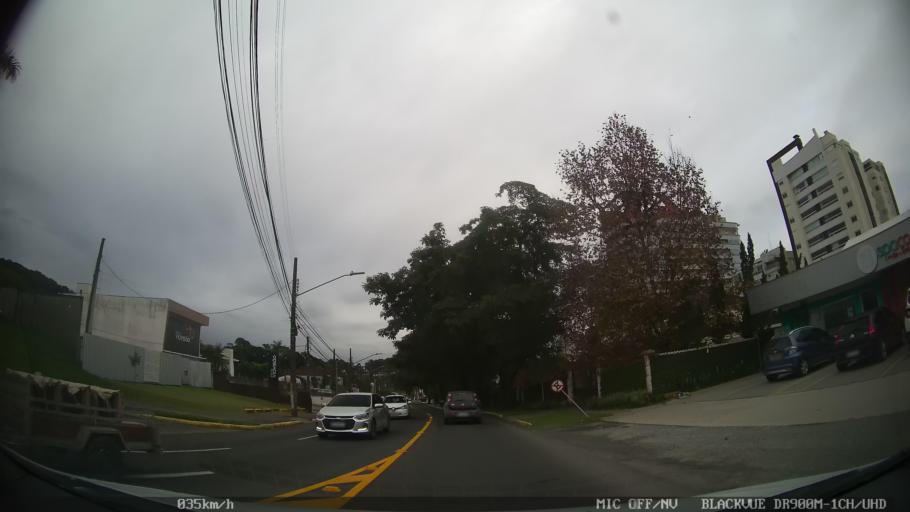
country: BR
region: Santa Catarina
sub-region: Joinville
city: Joinville
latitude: -26.3059
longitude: -48.8627
